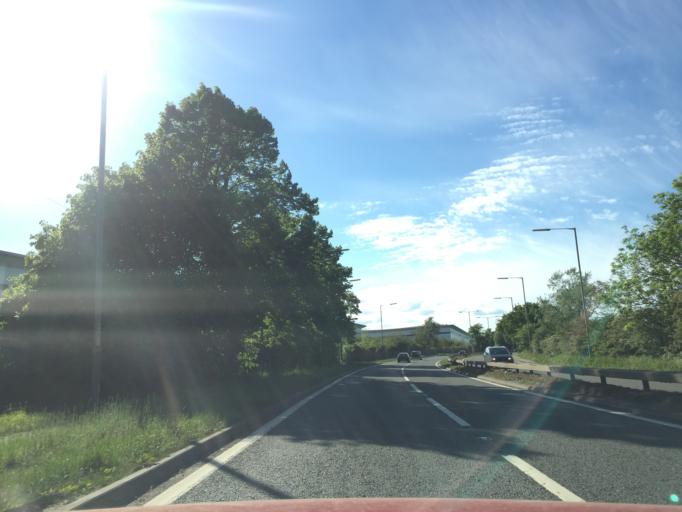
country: GB
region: England
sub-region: Warwickshire
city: Ryton on Dunsmore
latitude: 52.3671
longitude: -1.4400
